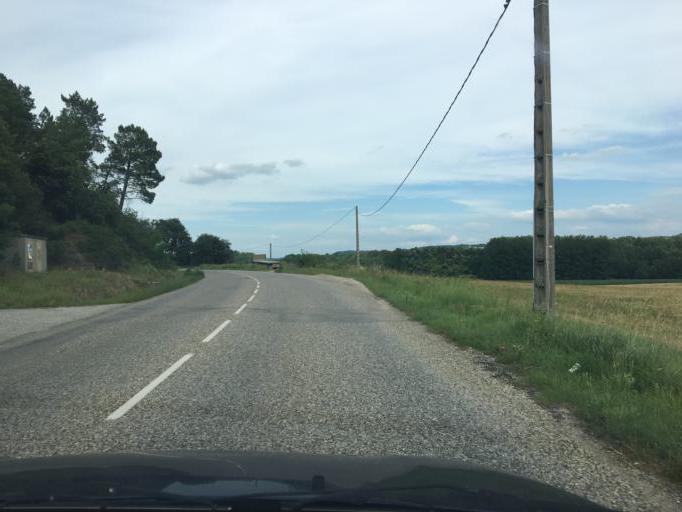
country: FR
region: Rhone-Alpes
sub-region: Departement de la Drome
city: Clerieux
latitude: 45.1093
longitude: 4.9543
